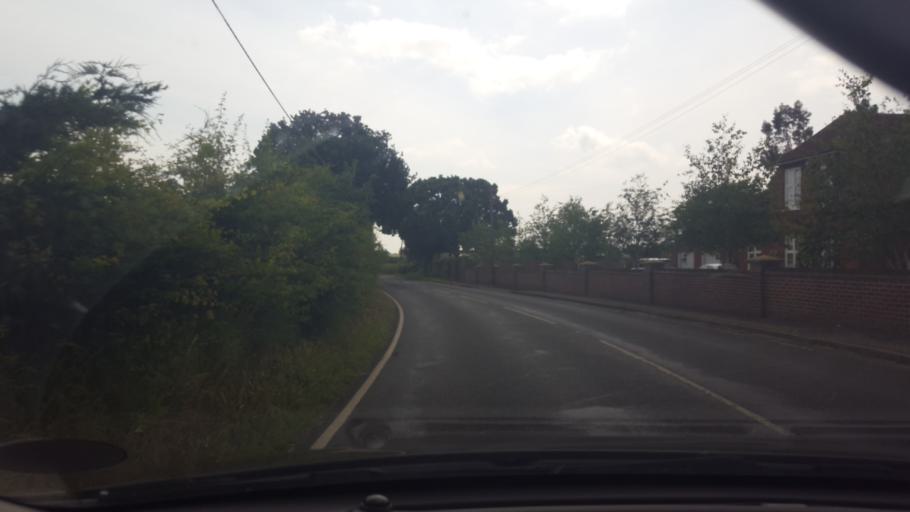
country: GB
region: England
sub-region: Essex
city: Mistley
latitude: 51.8939
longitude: 1.1024
